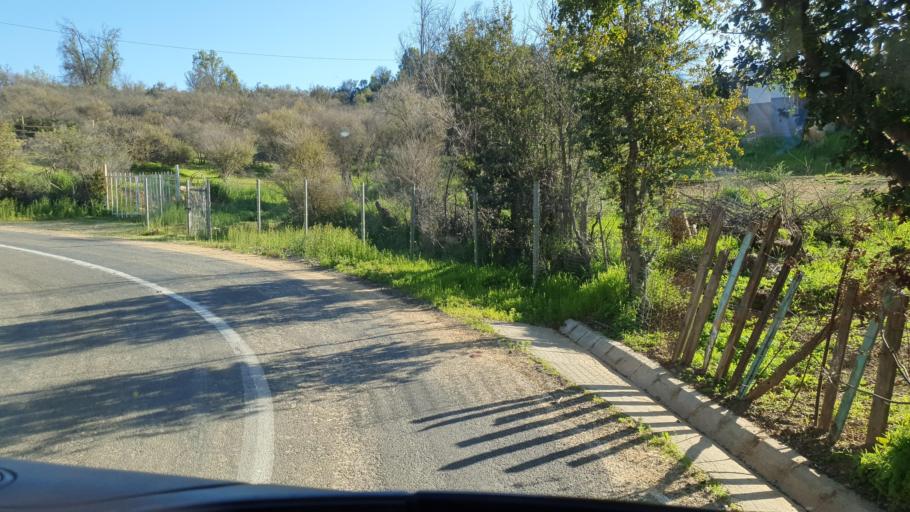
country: CL
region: Valparaiso
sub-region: Provincia de Marga Marga
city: Limache
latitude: -33.1798
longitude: -71.1854
